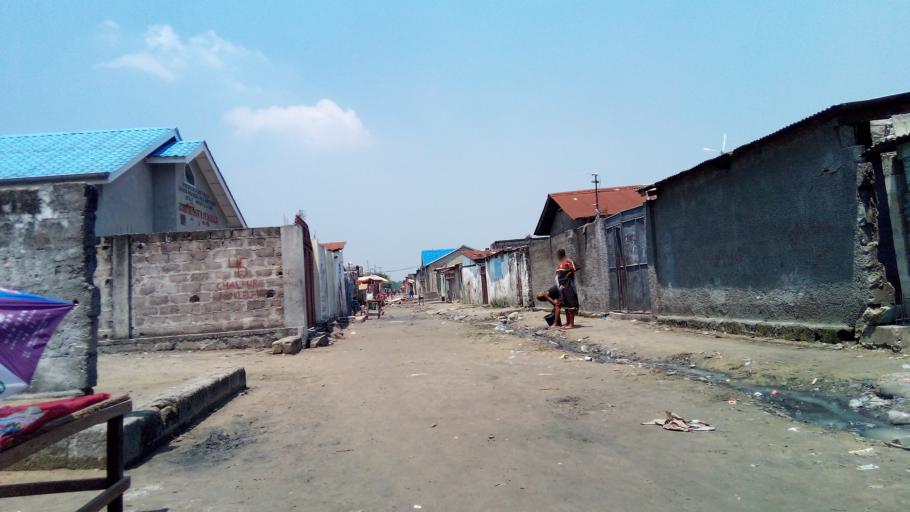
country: CD
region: Kinshasa
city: Kinshasa
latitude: -4.3672
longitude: 15.3081
